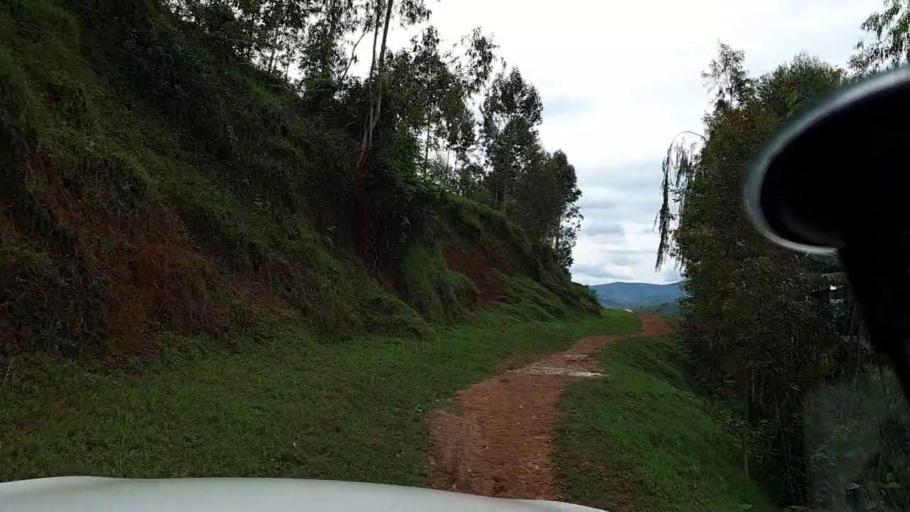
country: RW
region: Southern Province
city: Gitarama
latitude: -2.0764
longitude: 29.6436
